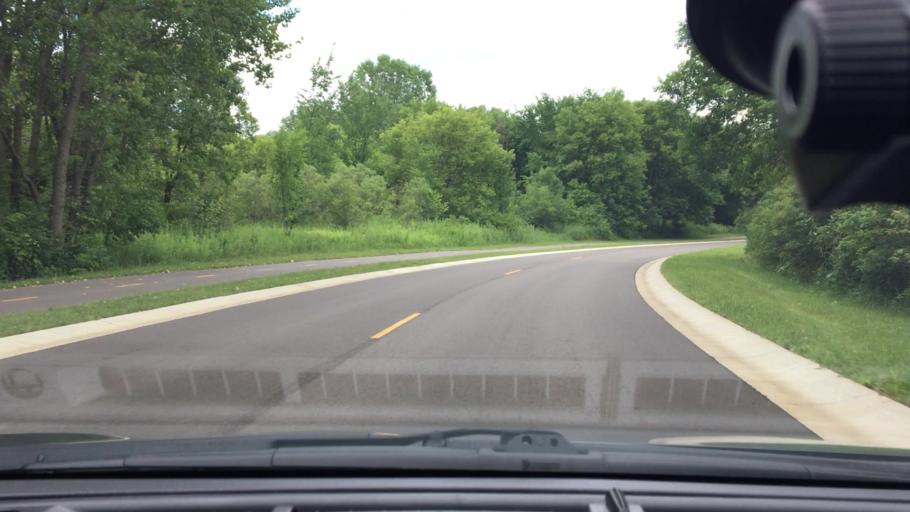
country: US
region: Minnesota
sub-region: Hennepin County
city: Plymouth
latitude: 45.0270
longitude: -93.4365
